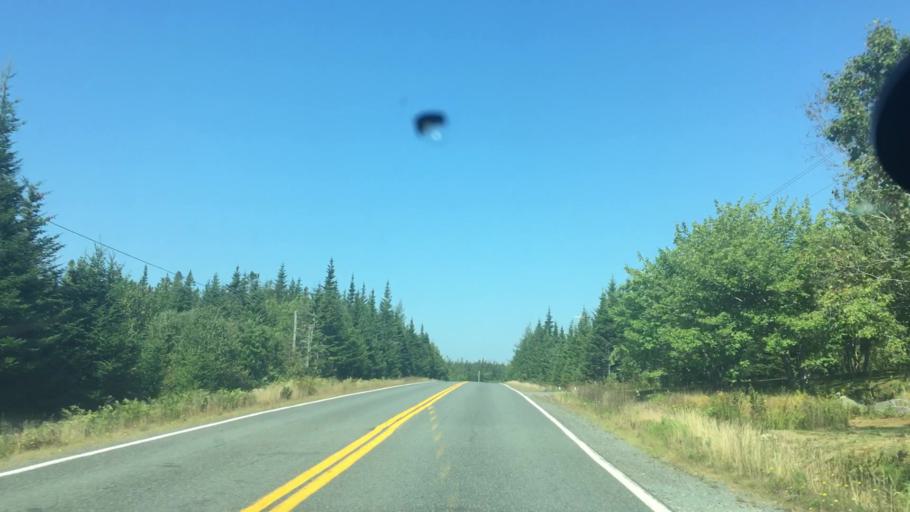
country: CA
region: Nova Scotia
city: Antigonish
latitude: 45.0042
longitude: -62.1027
